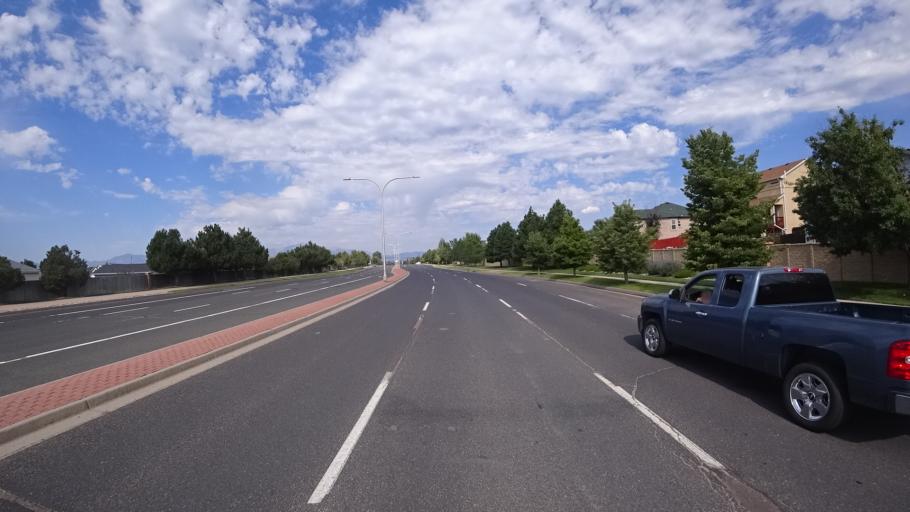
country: US
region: Colorado
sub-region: El Paso County
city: Cimarron Hills
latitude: 38.9124
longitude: -104.6913
